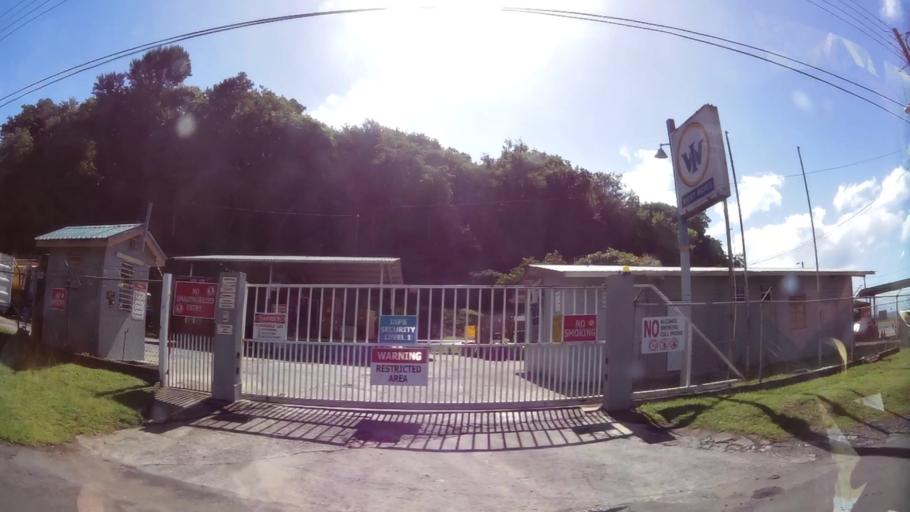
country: DM
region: Saint George
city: Roseau
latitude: 15.3281
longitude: -61.3946
